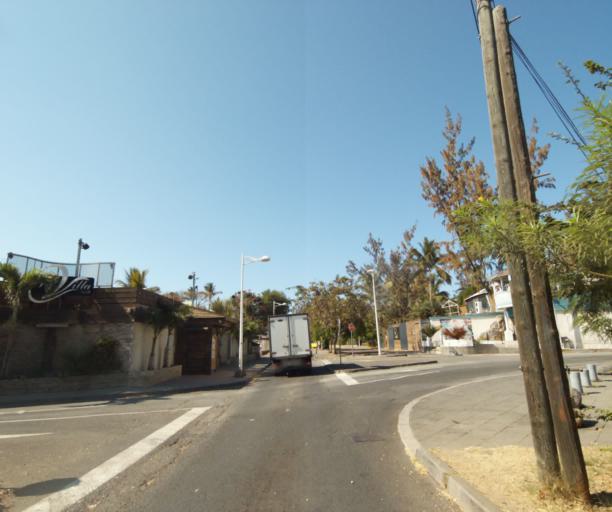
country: RE
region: Reunion
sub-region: Reunion
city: Saint-Paul
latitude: -21.0699
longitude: 55.2228
